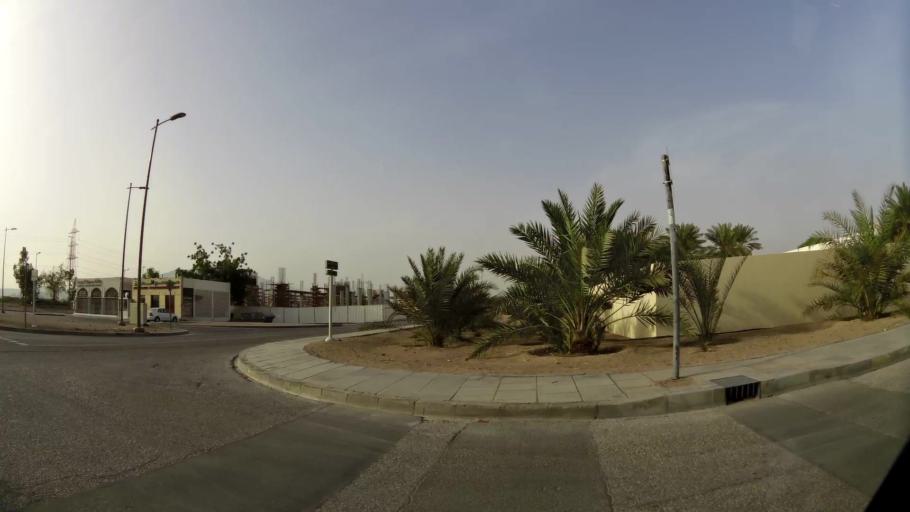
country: AE
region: Abu Dhabi
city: Al Ain
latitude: 24.1245
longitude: 55.7131
